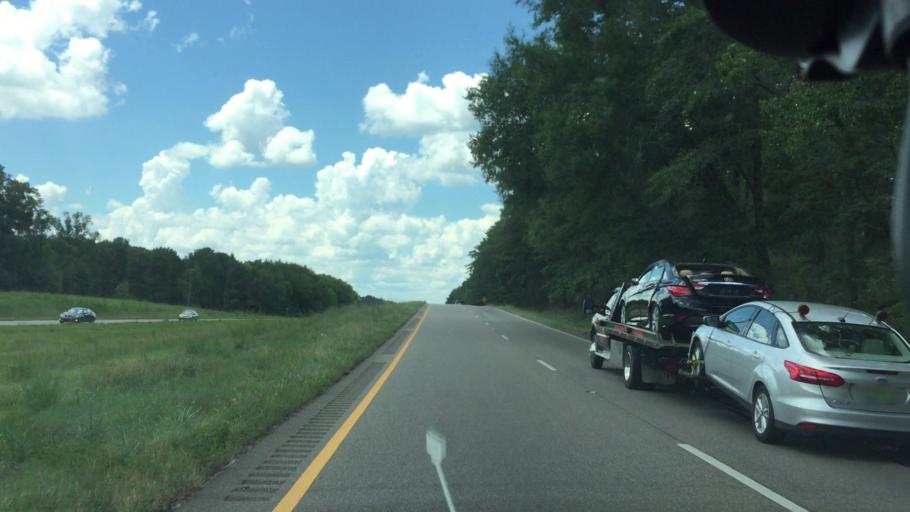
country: US
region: Alabama
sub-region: Montgomery County
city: Pike Road
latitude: 32.1410
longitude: -86.0962
